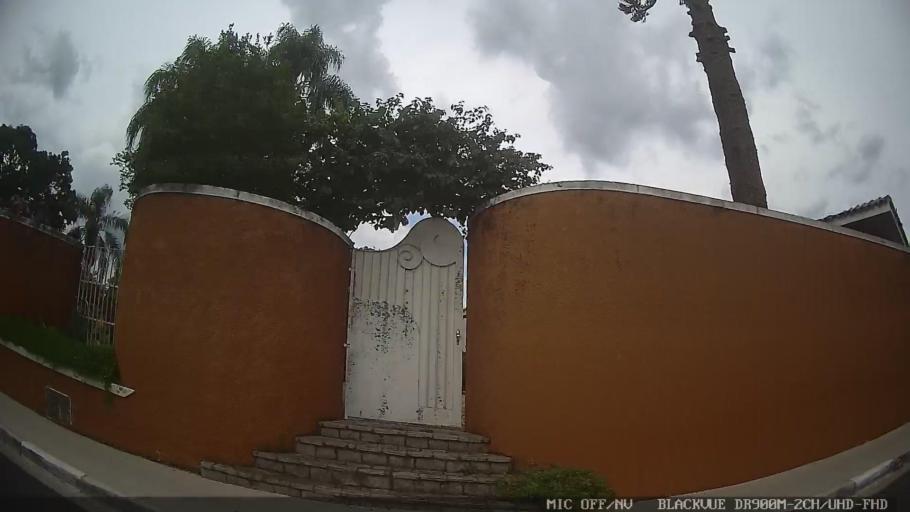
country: BR
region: Sao Paulo
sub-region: Atibaia
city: Atibaia
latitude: -23.1293
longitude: -46.5540
